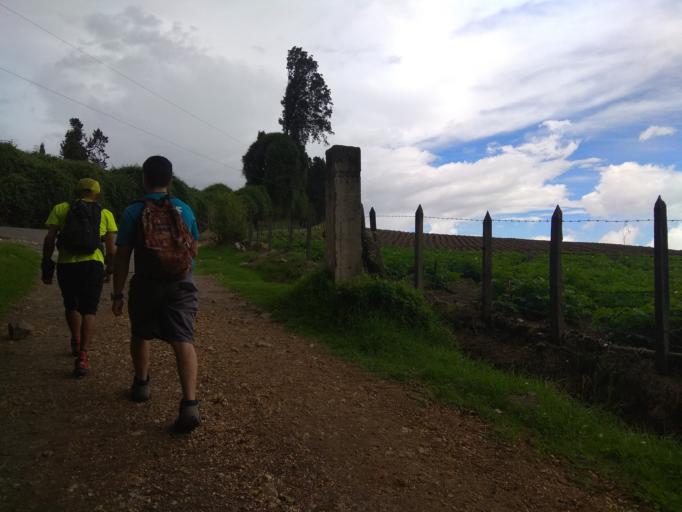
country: CR
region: Cartago
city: Cot
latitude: 9.9519
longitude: -83.8835
